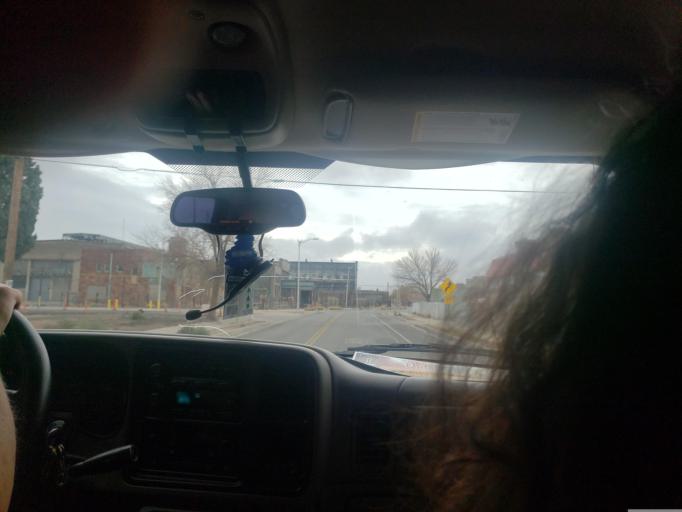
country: US
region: New Mexico
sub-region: Bernalillo County
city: Albuquerque
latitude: 35.0776
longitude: -106.6504
